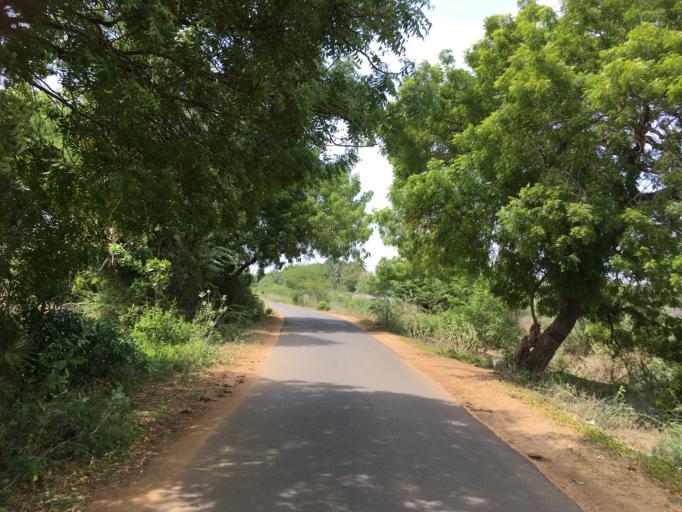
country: IN
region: Tamil Nadu
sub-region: Villupuram
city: Auroville
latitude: 12.0091
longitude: 79.7959
